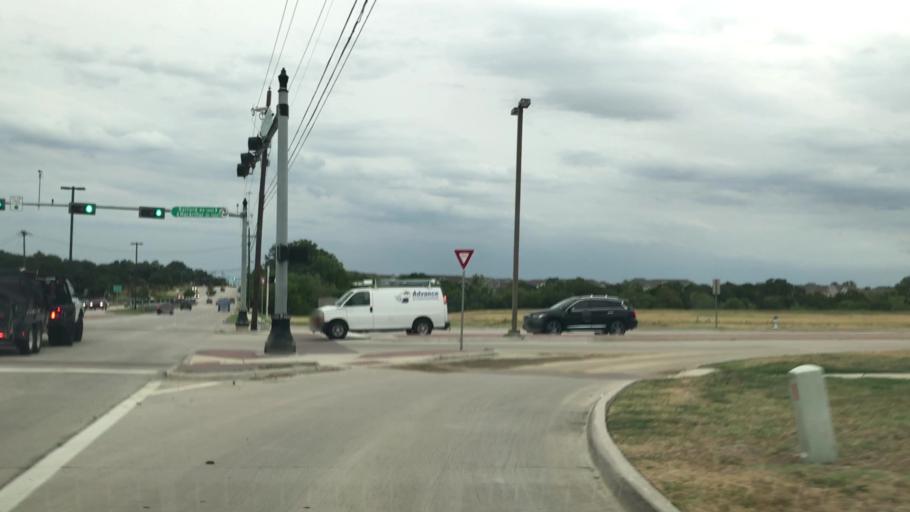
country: US
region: Texas
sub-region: Dallas County
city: Carrollton
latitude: 32.9875
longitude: -96.9097
